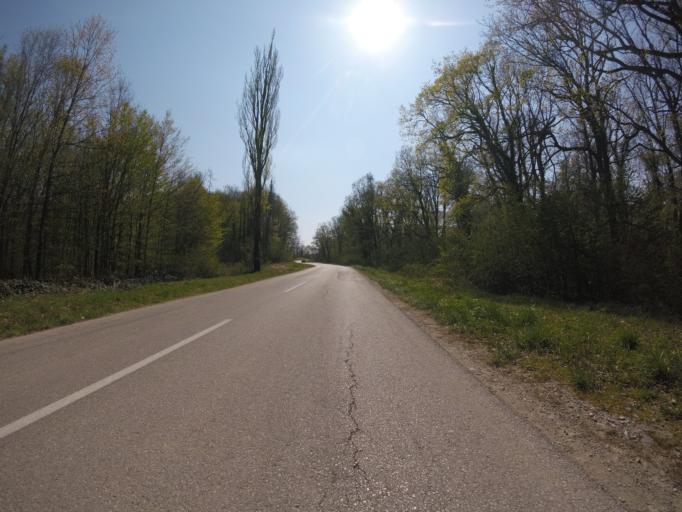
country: HR
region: Zagrebacka
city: Lukavec
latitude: 45.6304
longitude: 15.9617
